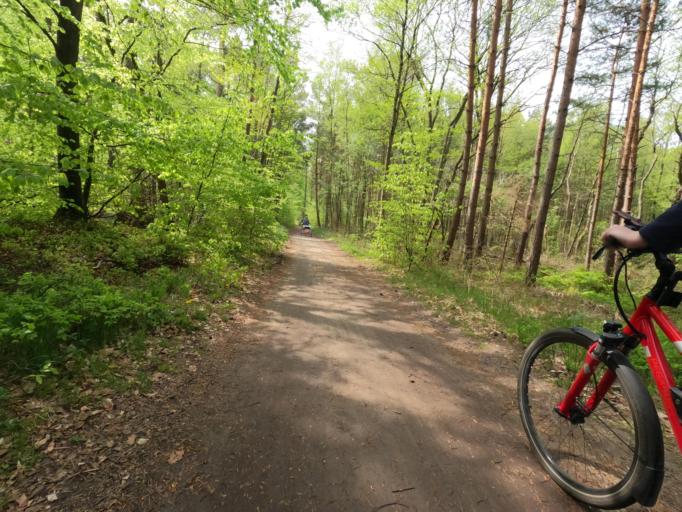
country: DE
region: Mecklenburg-Vorpommern
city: Ostseebad Prerow
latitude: 54.4473
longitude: 12.5452
